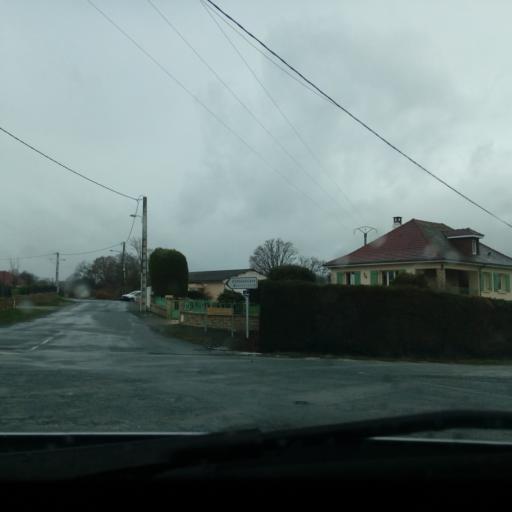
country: FR
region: Limousin
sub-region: Departement de la Creuse
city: Gueret
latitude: 46.1954
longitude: 1.8725
